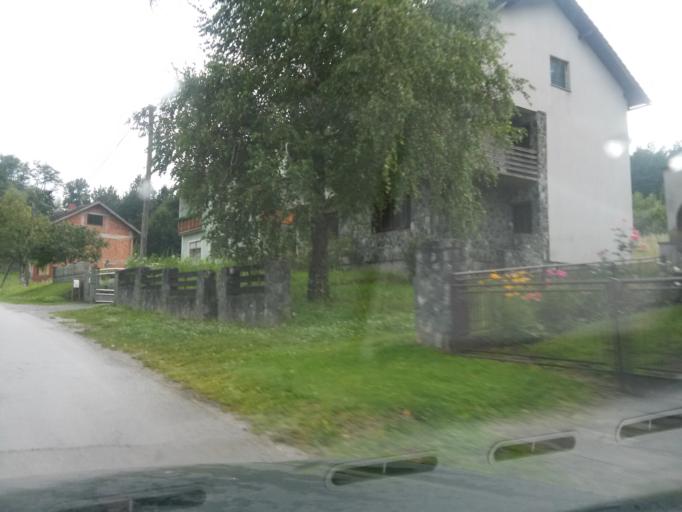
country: HR
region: Sisacko-Moslavacka
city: Gvozd
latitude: 45.2984
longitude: 15.9677
